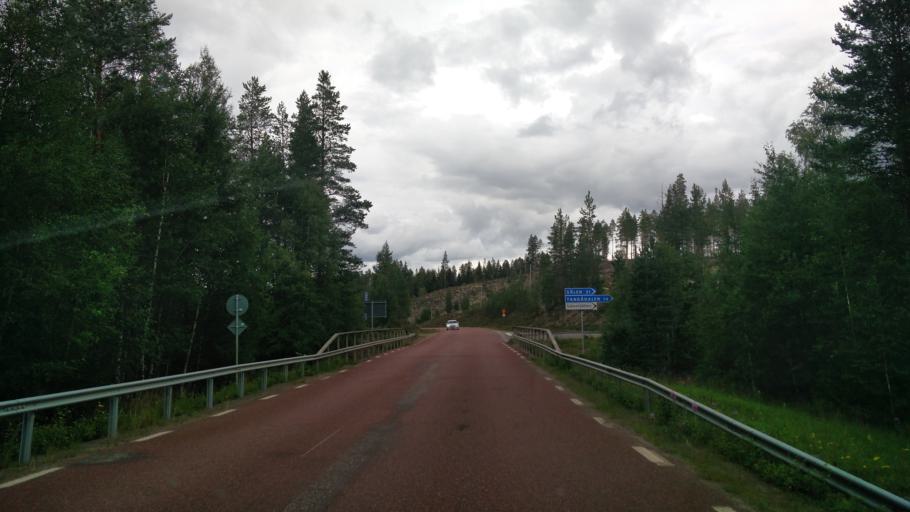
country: NO
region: Hedmark
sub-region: Trysil
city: Innbygda
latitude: 61.1513
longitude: 12.8012
